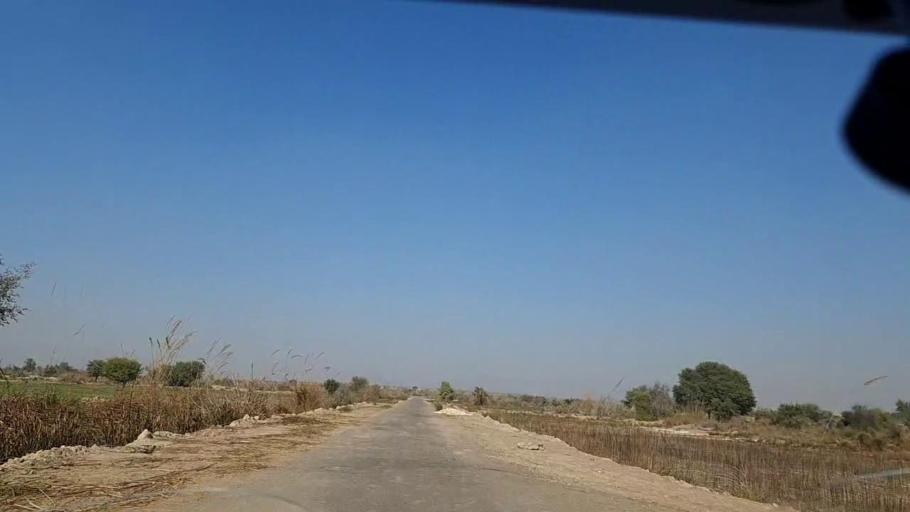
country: PK
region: Sindh
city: Khanpur
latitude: 27.5731
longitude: 69.3798
